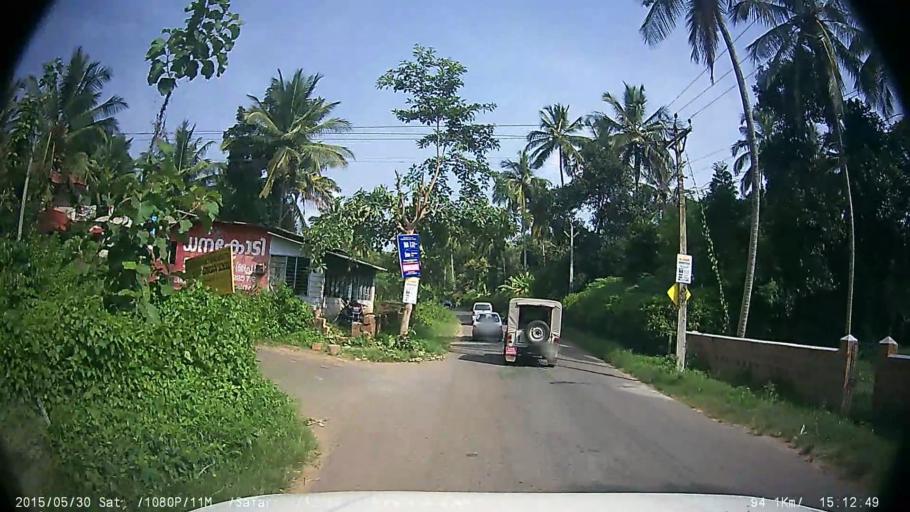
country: IN
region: Kerala
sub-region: Wayanad
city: Panamaram
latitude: 11.7941
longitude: 76.0408
